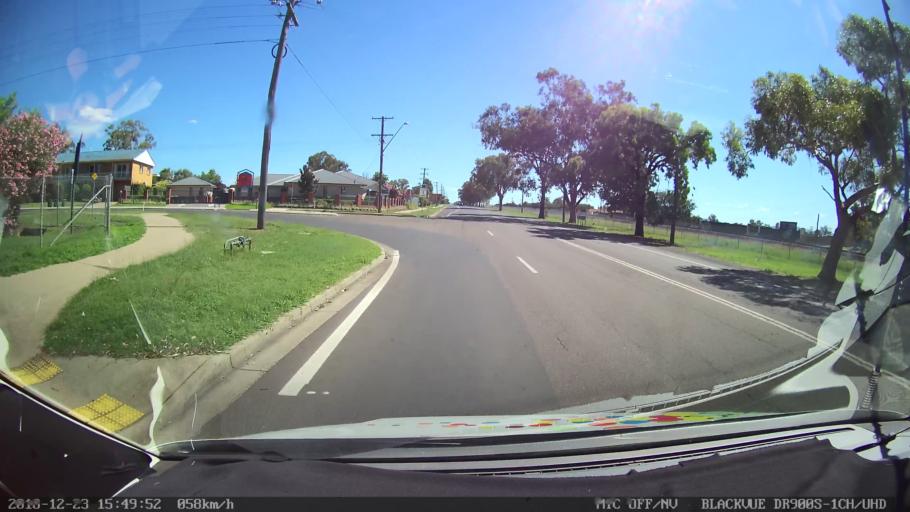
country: AU
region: New South Wales
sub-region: Tamworth Municipality
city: South Tamworth
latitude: -31.1021
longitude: 150.9038
